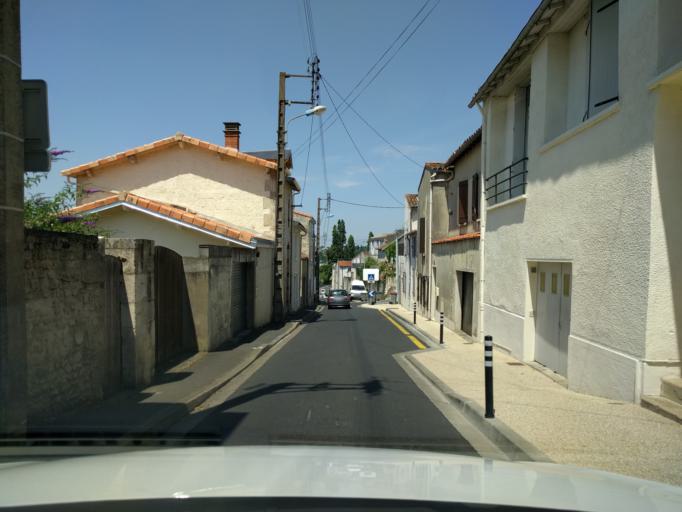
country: FR
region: Poitou-Charentes
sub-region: Departement des Deux-Sevres
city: Niort
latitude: 46.3353
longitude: -0.4625
